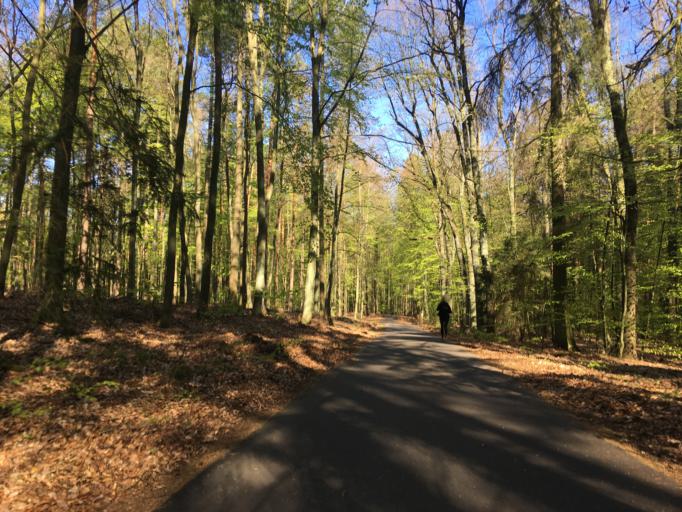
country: DE
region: Brandenburg
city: Wandlitz
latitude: 52.7388
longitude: 13.4967
